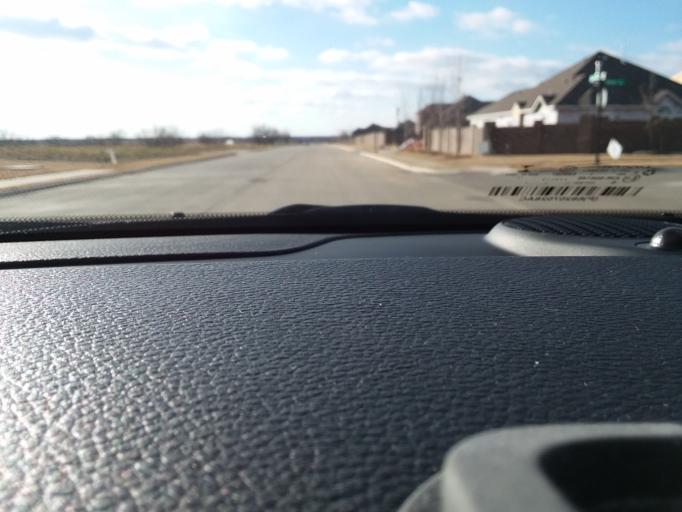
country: US
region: Texas
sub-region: Collin County
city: Prosper
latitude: 33.2658
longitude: -96.8871
